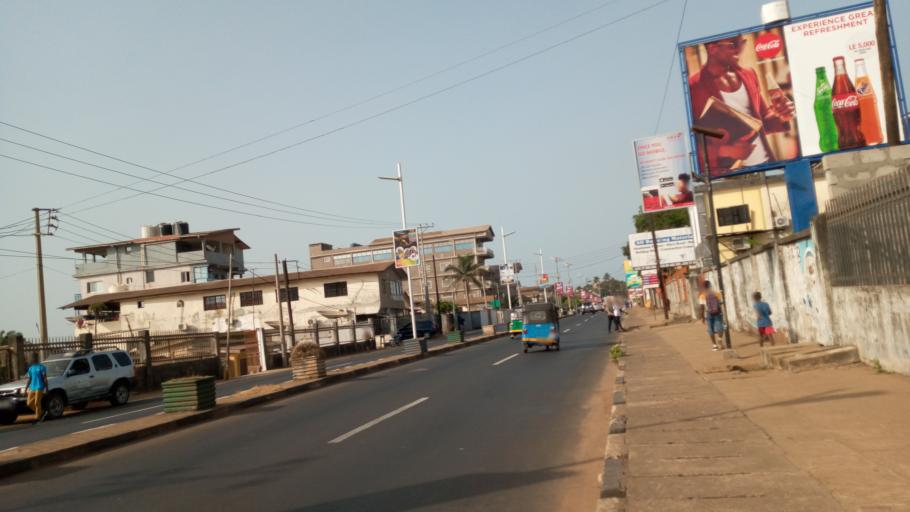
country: SL
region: Western Area
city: Freetown
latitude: 8.4817
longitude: -13.2693
